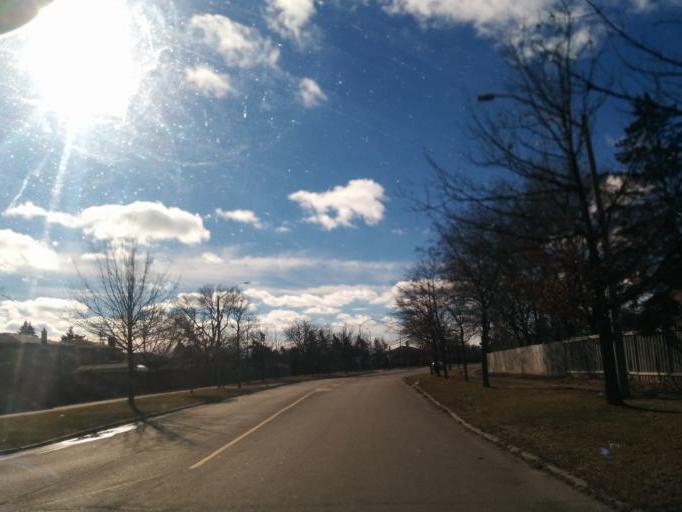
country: CA
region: Ontario
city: Mississauga
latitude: 43.5646
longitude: -79.6273
